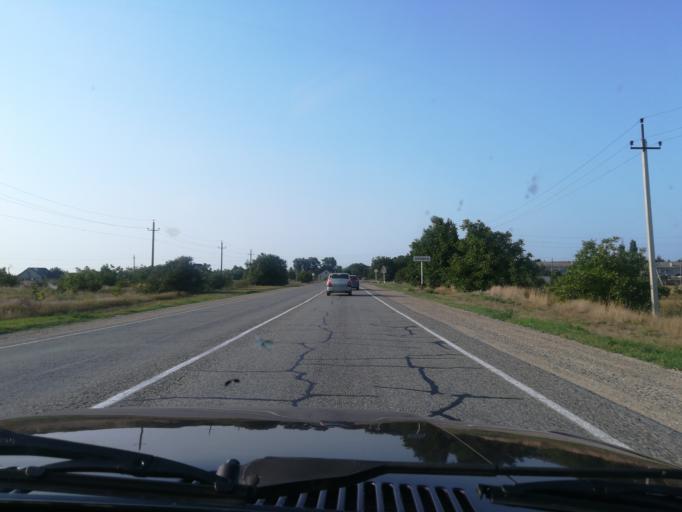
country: RU
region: Krasnodarskiy
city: Yurovka
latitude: 45.1091
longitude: 37.4219
